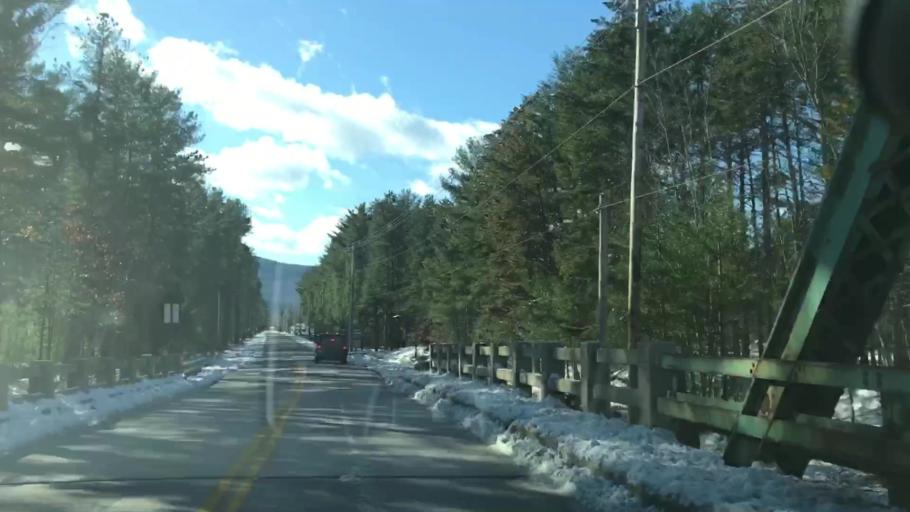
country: US
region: Maine
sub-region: Oxford County
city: Brownfield
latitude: 43.9552
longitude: -70.8825
